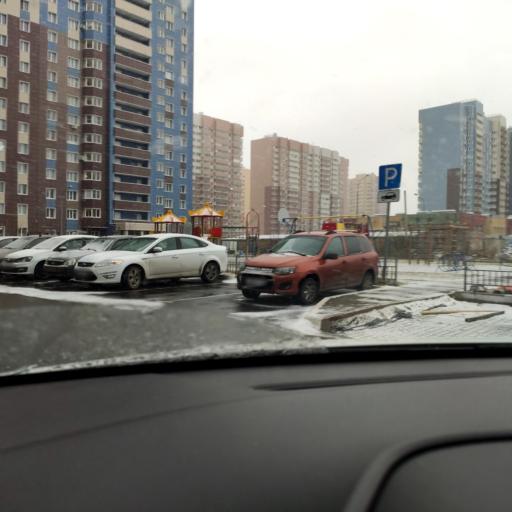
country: RU
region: Tatarstan
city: Osinovo
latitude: 55.8673
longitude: 48.8790
